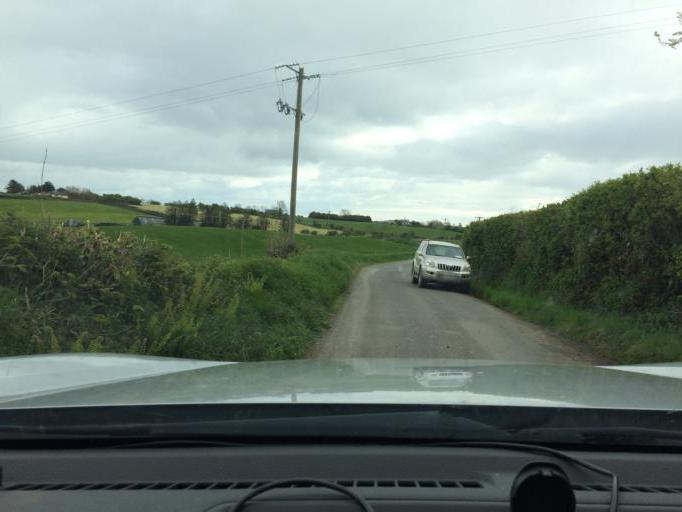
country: IE
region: Munster
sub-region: Waterford
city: Dungarvan
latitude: 52.0545
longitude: -7.6170
